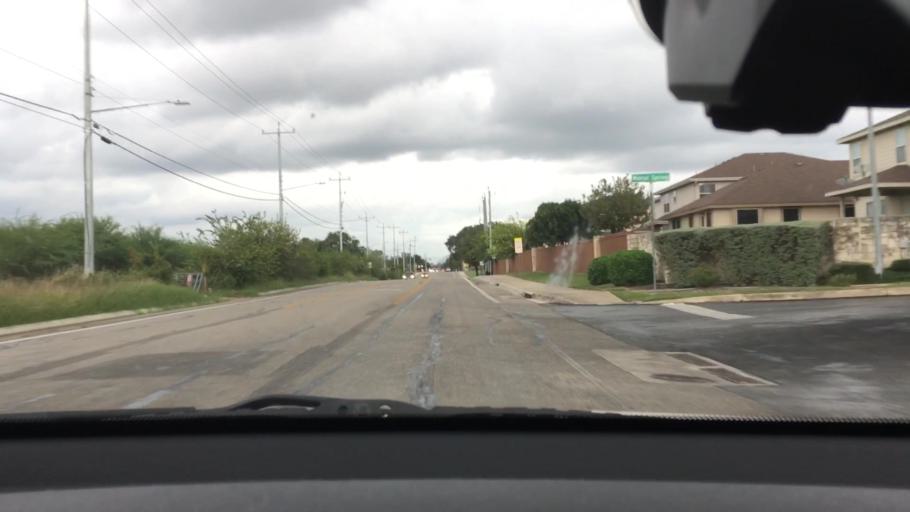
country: US
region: Texas
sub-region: Bexar County
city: Converse
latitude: 29.5327
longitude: -98.3126
